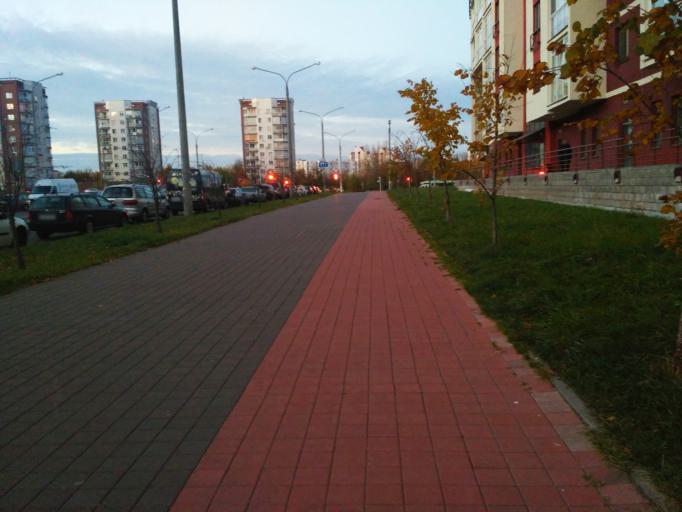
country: BY
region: Minsk
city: Novoye Medvezhino
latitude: 53.8708
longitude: 27.4864
